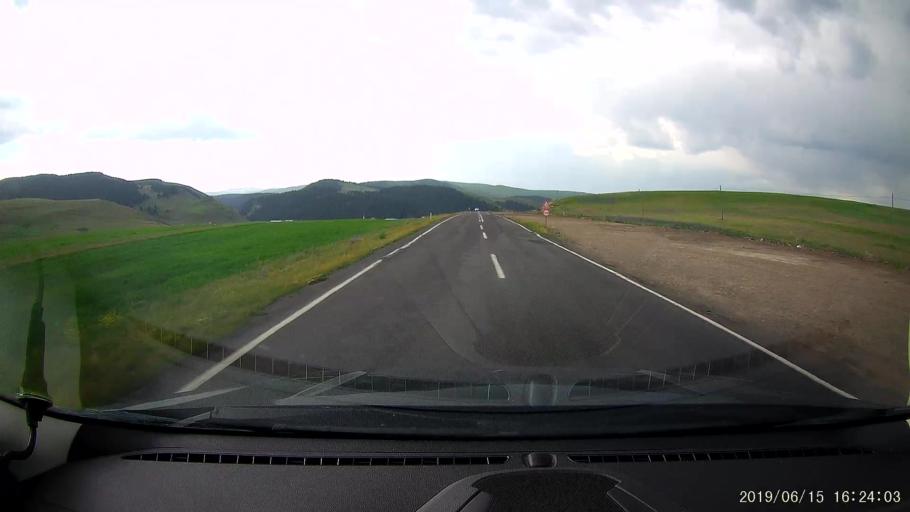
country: TR
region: Ardahan
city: Hanak
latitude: 41.1700
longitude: 42.8681
